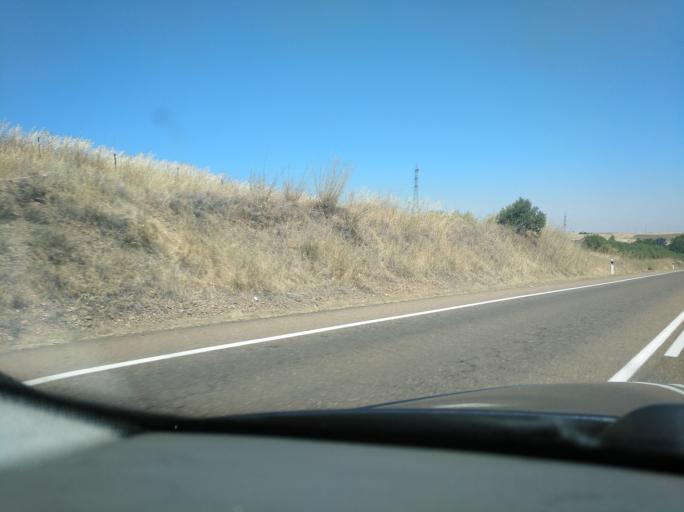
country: ES
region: Extremadura
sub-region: Provincia de Badajoz
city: Olivenza
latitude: 38.7325
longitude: -7.0703
